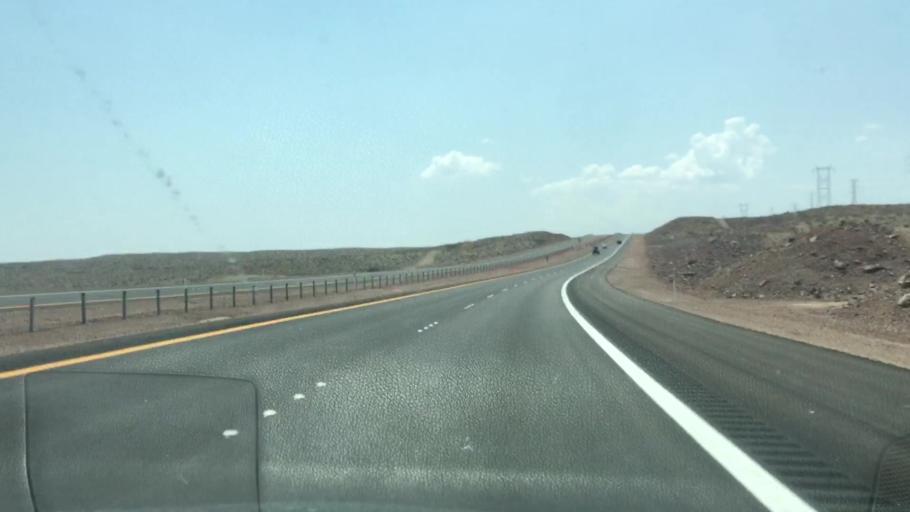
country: US
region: Nevada
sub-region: Clark County
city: Boulder City
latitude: 35.9749
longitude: -114.7930
